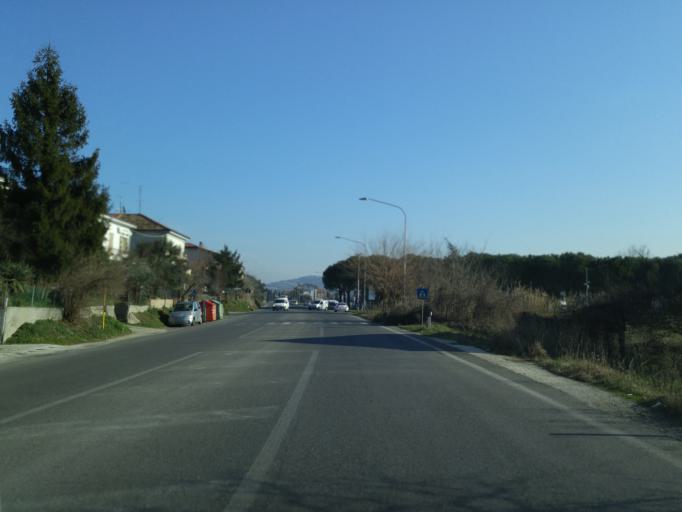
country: IT
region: The Marches
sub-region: Provincia di Pesaro e Urbino
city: Gabicce Mare
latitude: 43.9555
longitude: 12.7686
